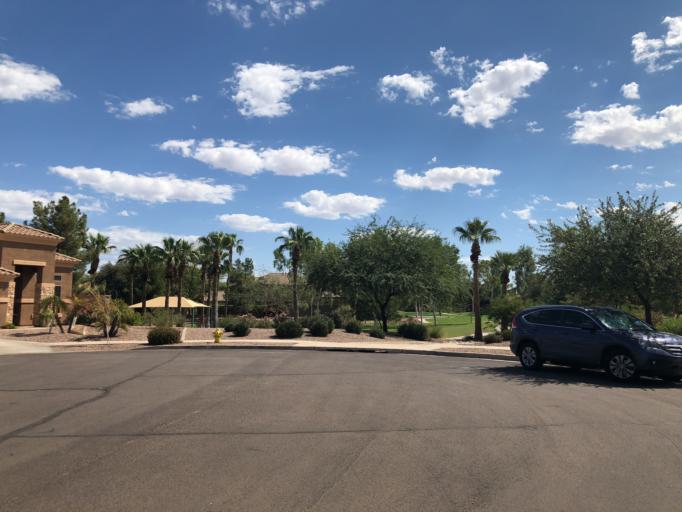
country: US
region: Arizona
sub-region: Maricopa County
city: Queen Creek
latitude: 33.2752
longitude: -111.6945
